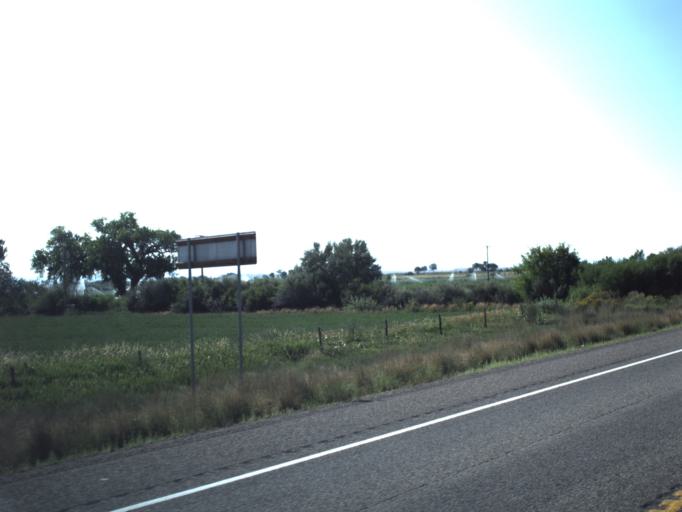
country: US
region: Utah
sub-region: Emery County
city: Castle Dale
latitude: 39.2066
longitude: -111.0243
